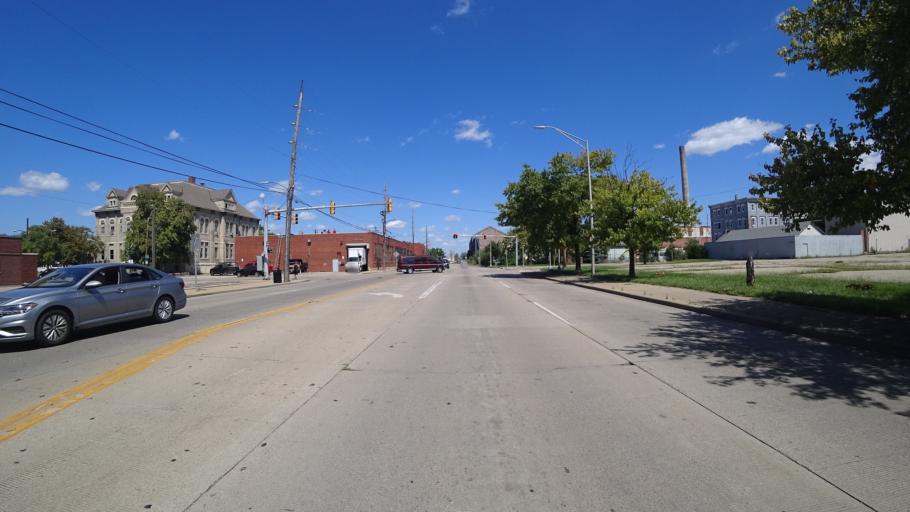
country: US
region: Ohio
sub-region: Butler County
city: Hamilton
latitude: 39.4005
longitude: -84.5579
